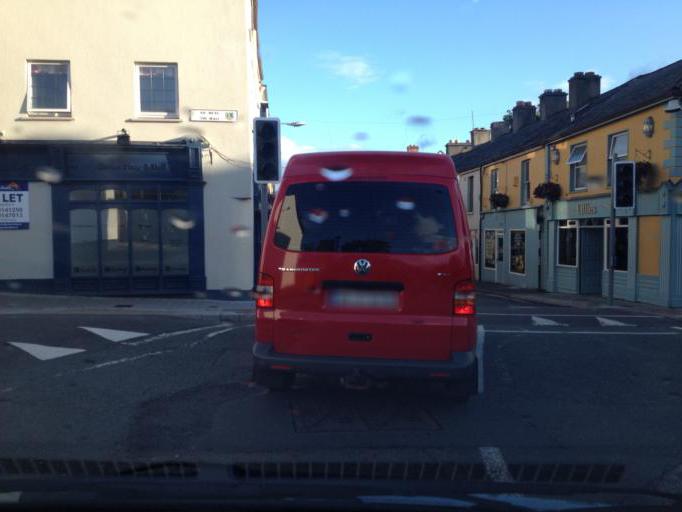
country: IE
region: Connaught
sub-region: Sligo
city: Sligo
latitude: 54.2727
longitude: -8.4715
